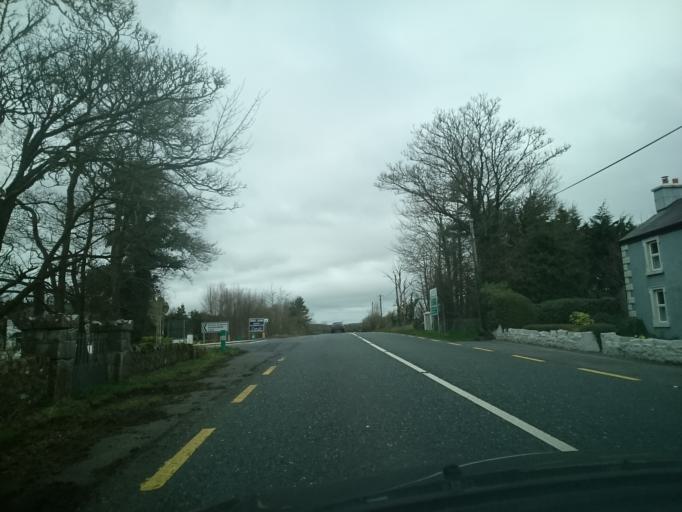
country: IE
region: Connaught
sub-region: Maigh Eo
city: Castlebar
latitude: 53.8199
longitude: -9.3723
